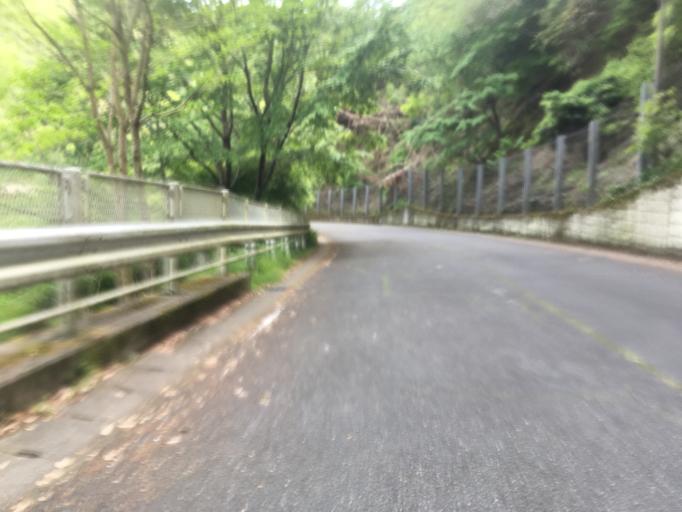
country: JP
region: Kyoto
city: Kameoka
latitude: 35.0242
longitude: 135.6385
